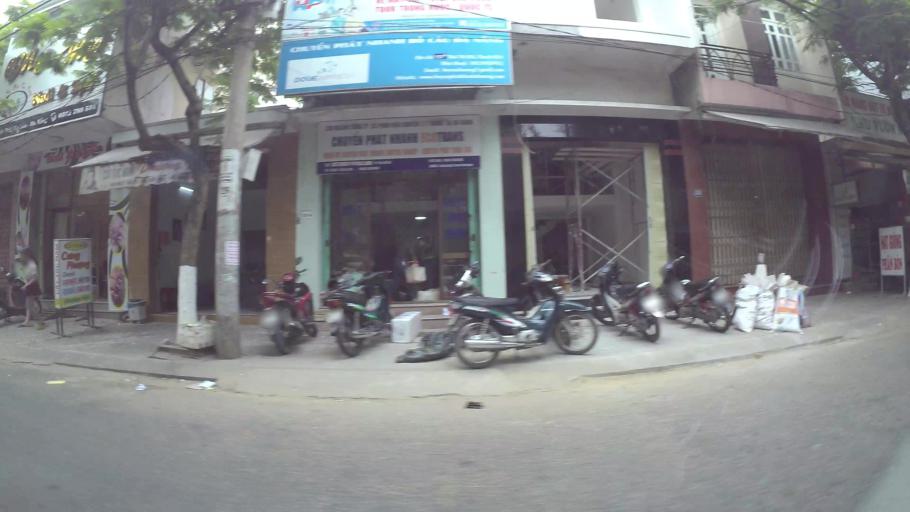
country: VN
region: Da Nang
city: Thanh Khe
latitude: 16.0684
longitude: 108.1969
